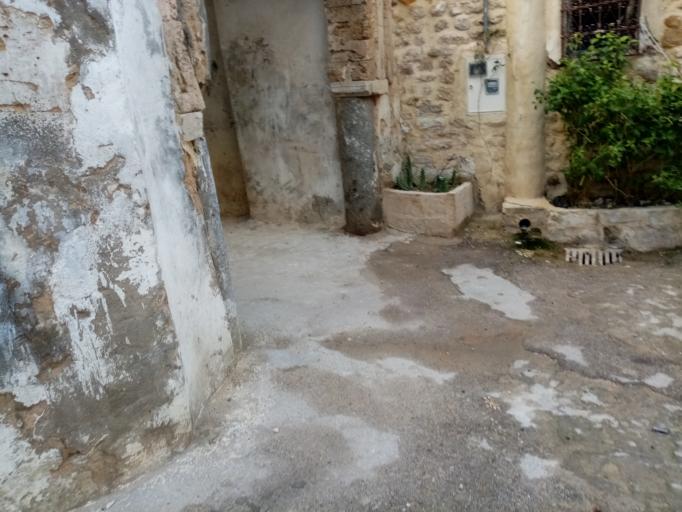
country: TN
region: Tunis
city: Tunis
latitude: 36.7941
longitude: 10.1670
